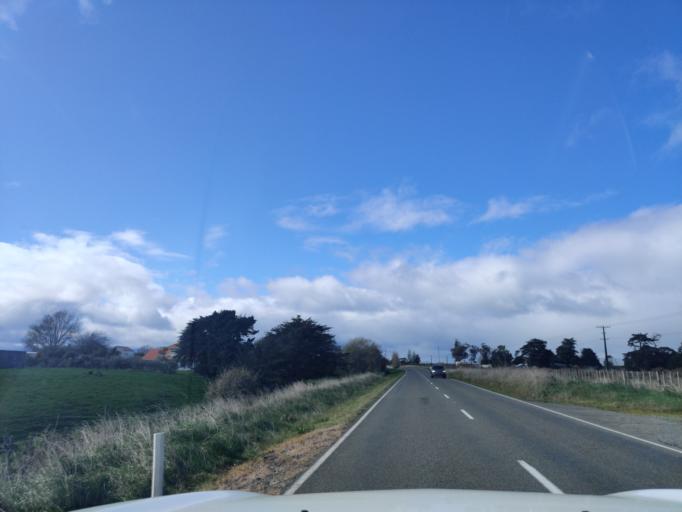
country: NZ
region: Manawatu-Wanganui
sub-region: Palmerston North City
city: Palmerston North
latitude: -40.2875
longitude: 175.6753
